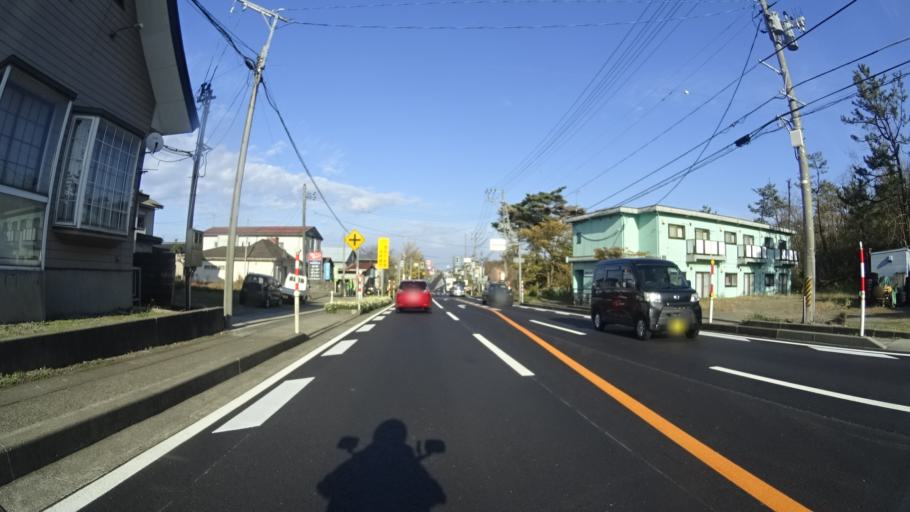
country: JP
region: Niigata
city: Joetsu
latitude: 37.2364
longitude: 138.3405
